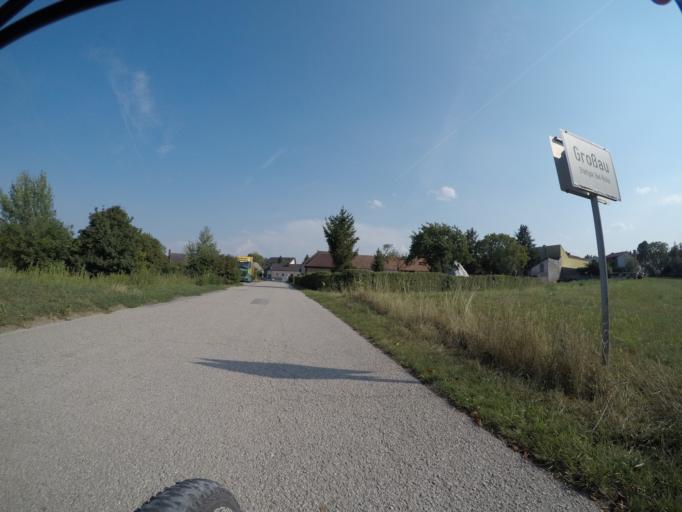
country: AT
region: Lower Austria
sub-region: Politischer Bezirk Baden
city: Hirtenberg
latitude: 47.9577
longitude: 16.1696
